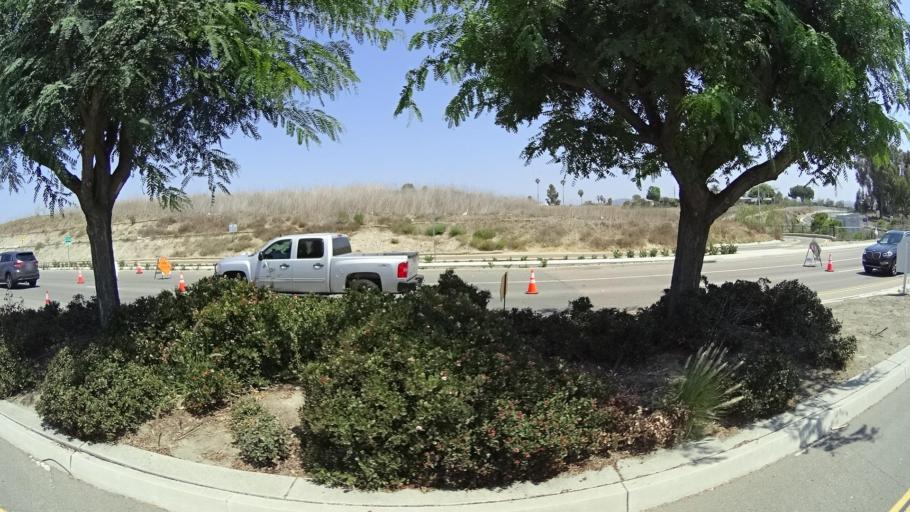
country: US
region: California
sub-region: San Diego County
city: Vista
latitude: 33.2201
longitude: -117.2585
